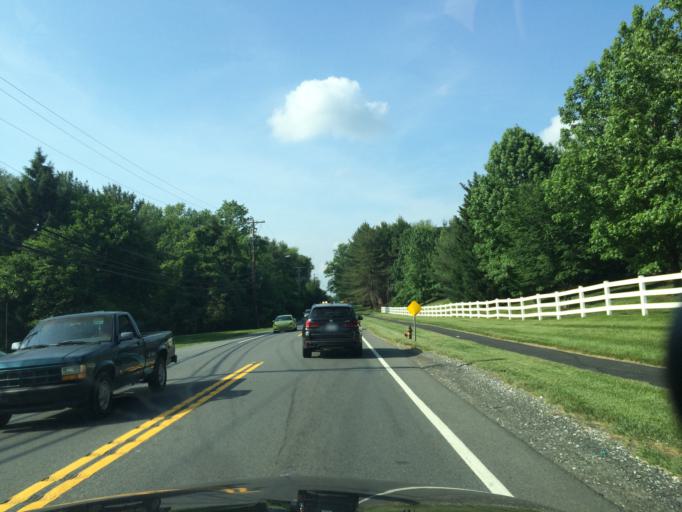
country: US
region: Maryland
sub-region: Montgomery County
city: Olney
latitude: 39.1685
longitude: -77.0598
